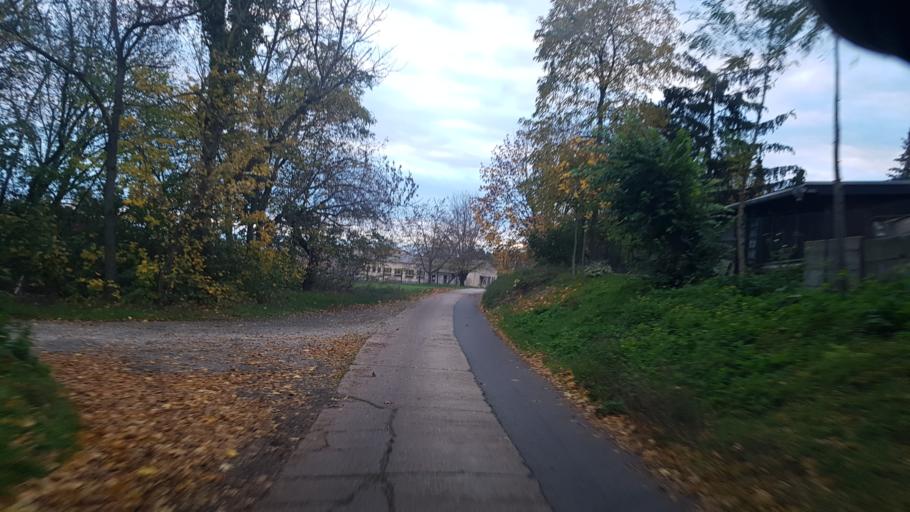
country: DE
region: Brandenburg
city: Muhlberg
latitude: 51.4516
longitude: 13.2315
